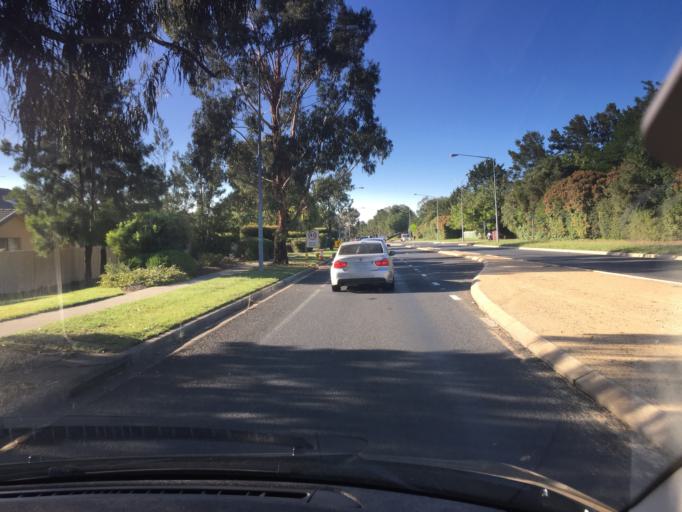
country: AU
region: Australian Capital Territory
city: Kaleen
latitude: -35.2357
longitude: 149.1253
